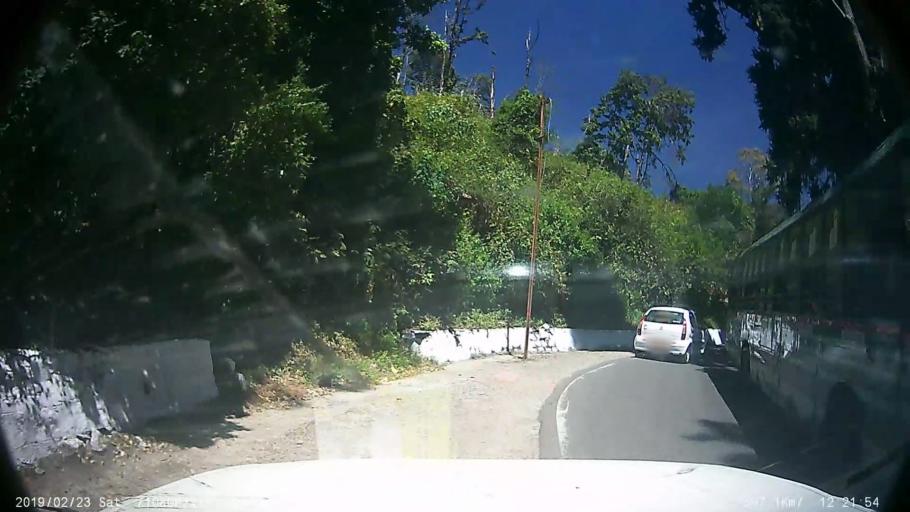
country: IN
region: Tamil Nadu
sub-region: Nilgiri
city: Wellington
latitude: 11.3375
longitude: 76.7983
